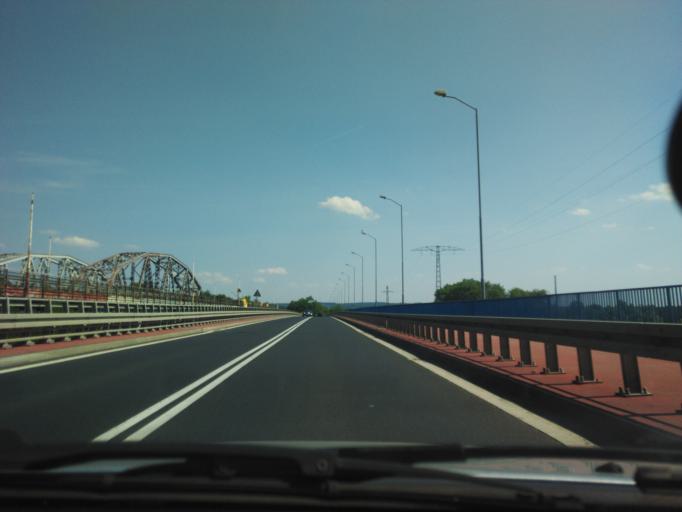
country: PL
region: West Pomeranian Voivodeship
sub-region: Szczecin
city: Szczecin
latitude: 53.3831
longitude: 14.5341
